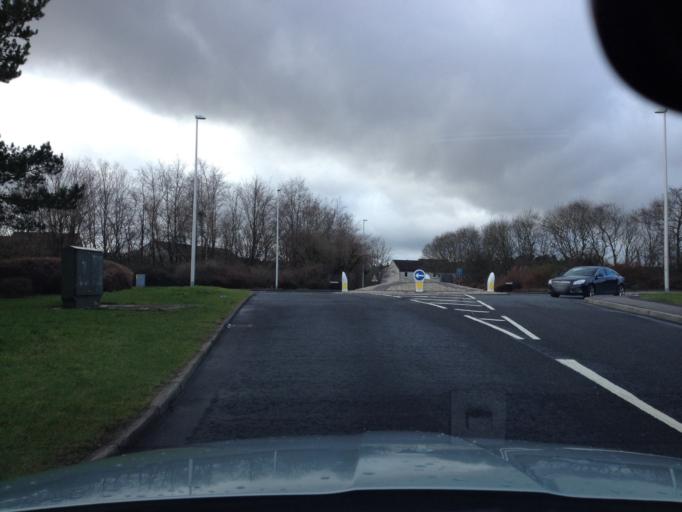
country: GB
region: Scotland
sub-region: West Lothian
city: Livingston
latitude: 55.9053
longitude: -3.5322
